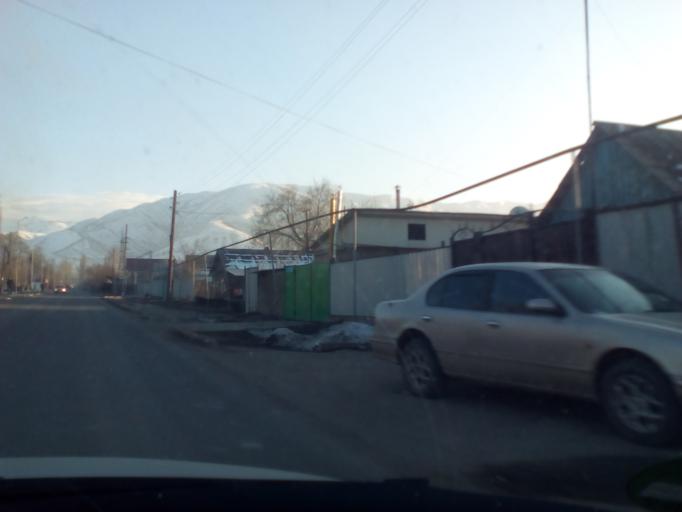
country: KZ
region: Almaty Oblysy
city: Burunday
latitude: 43.1716
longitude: 76.4159
